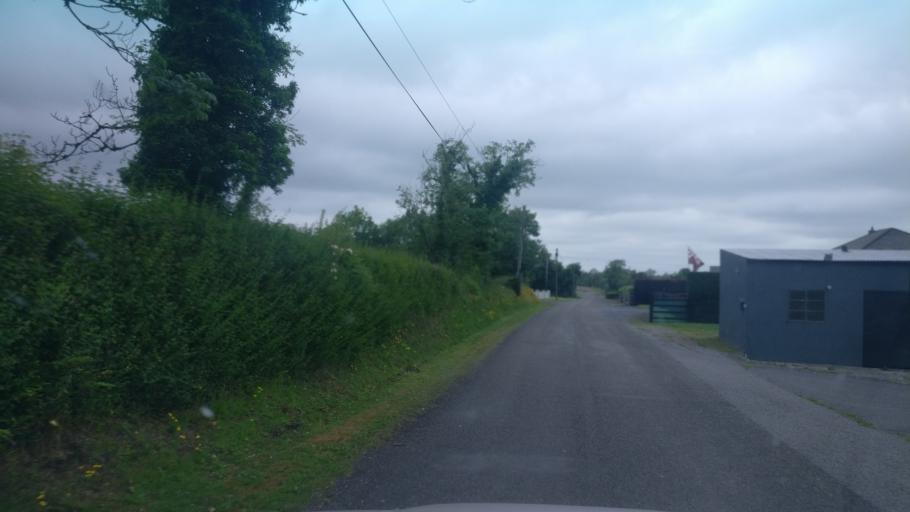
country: IE
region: Connaught
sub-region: County Galway
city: Ballinasloe
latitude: 53.2958
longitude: -8.3412
